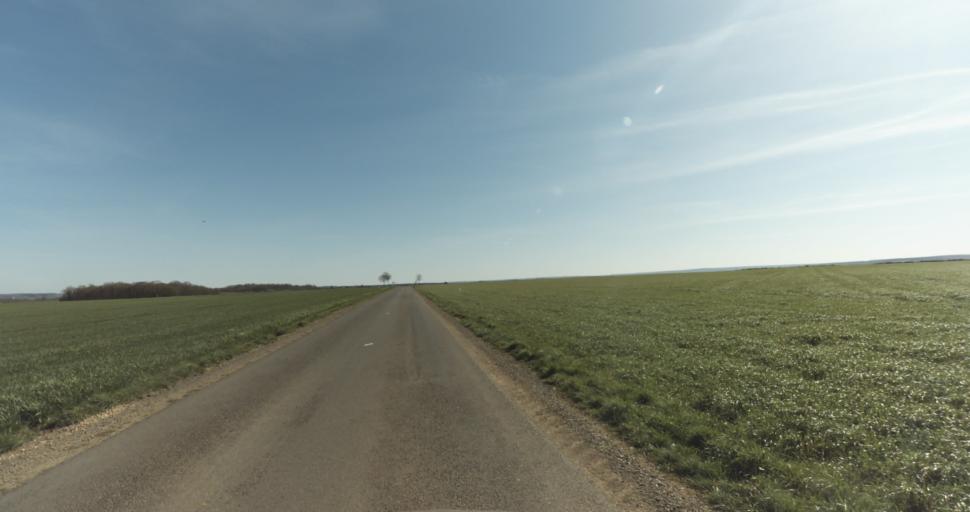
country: FR
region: Lower Normandy
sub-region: Departement du Calvados
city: Saint-Pierre-sur-Dives
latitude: 48.9952
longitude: -0.0461
